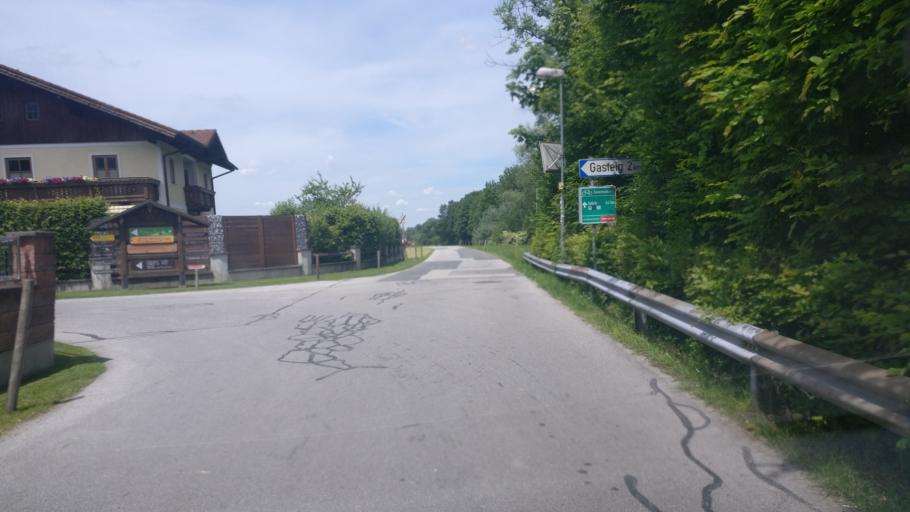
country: AT
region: Salzburg
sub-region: Politischer Bezirk Hallein
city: Kuchl
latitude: 47.6259
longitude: 13.1379
